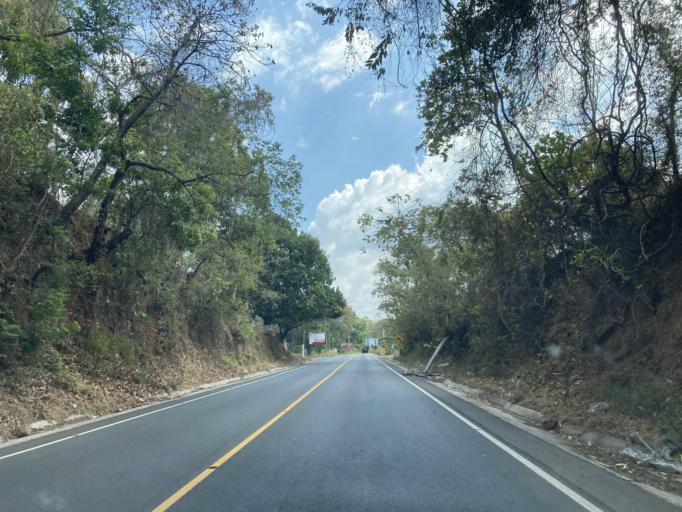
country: GT
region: Santa Rosa
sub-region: Municipio de Taxisco
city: Taxisco
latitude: 14.0646
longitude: -90.4542
